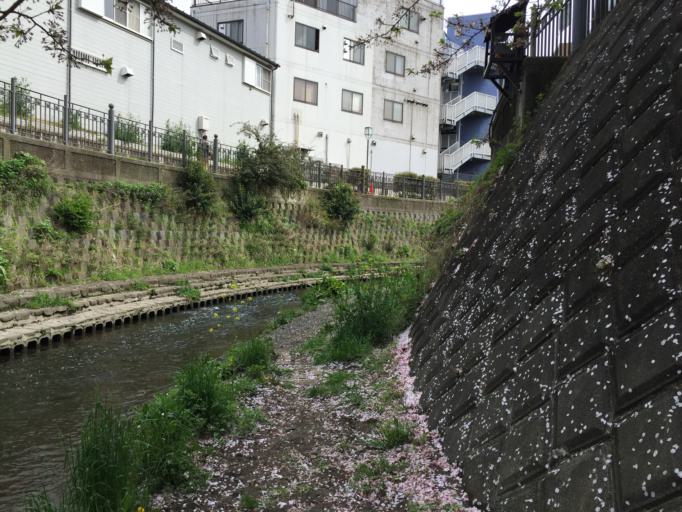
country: JP
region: Kanagawa
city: Yokohama
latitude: 35.4078
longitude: 139.5939
